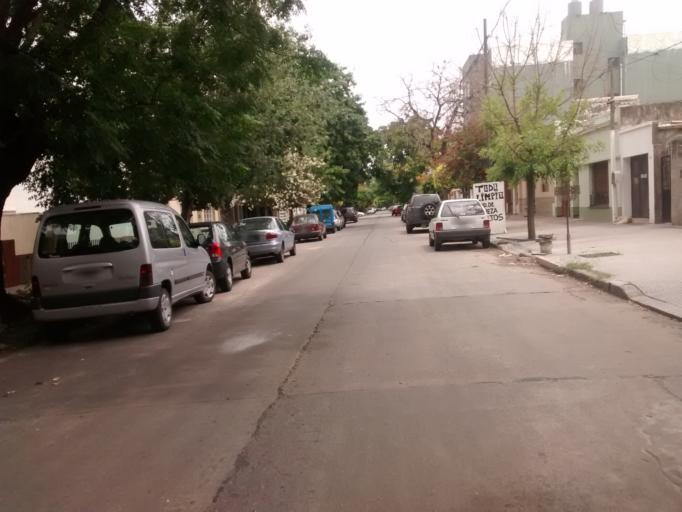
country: AR
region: Buenos Aires
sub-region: Partido de La Plata
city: La Plata
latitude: -34.9330
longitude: -57.9344
